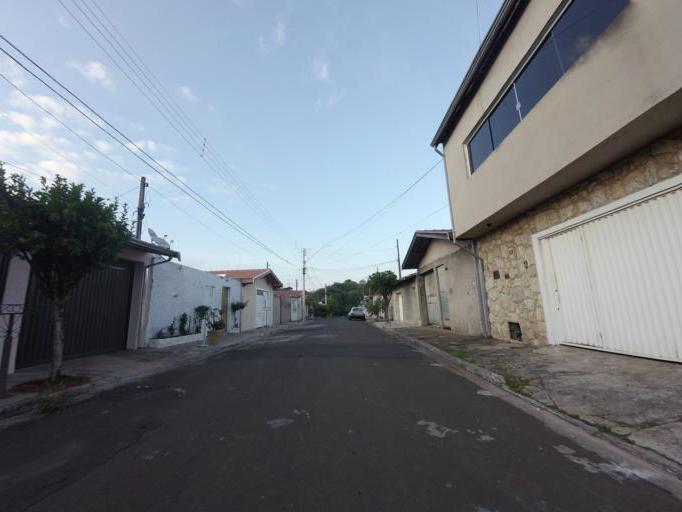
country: BR
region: Sao Paulo
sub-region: Piracicaba
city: Piracicaba
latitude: -22.7572
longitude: -47.6087
